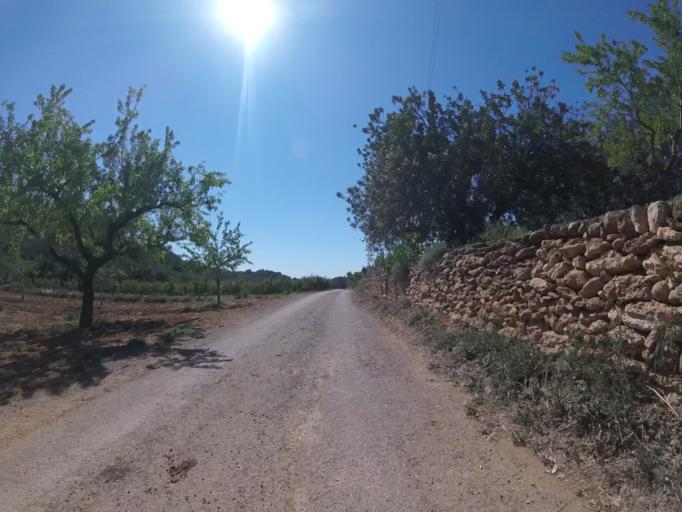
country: ES
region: Valencia
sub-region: Provincia de Castello
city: Cuevas de Vinroma
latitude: 40.3717
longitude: 0.1344
